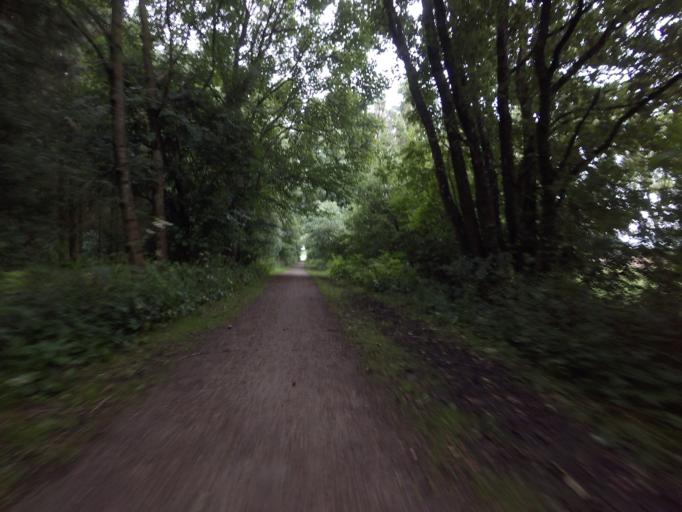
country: DK
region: North Denmark
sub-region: Alborg Kommune
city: Vadum
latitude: 57.1151
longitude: 9.8763
